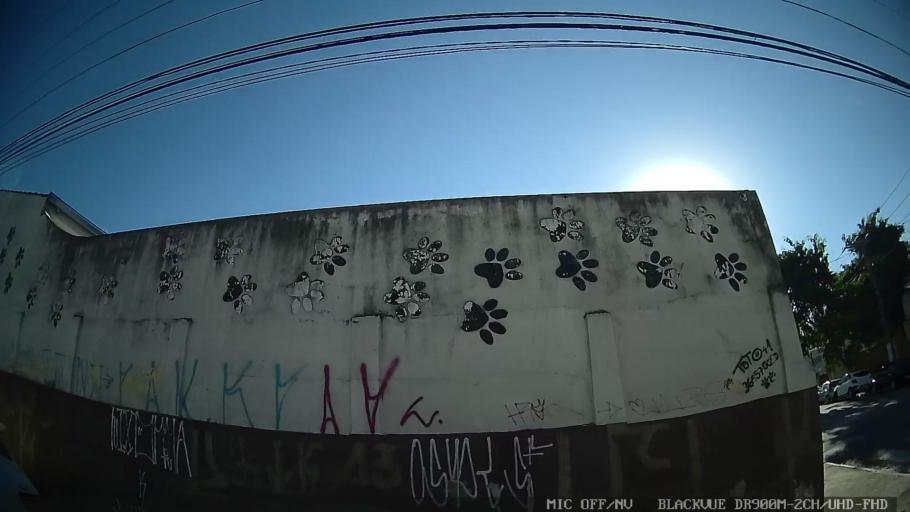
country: BR
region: Sao Paulo
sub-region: Guarulhos
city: Guarulhos
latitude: -23.5336
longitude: -46.5215
